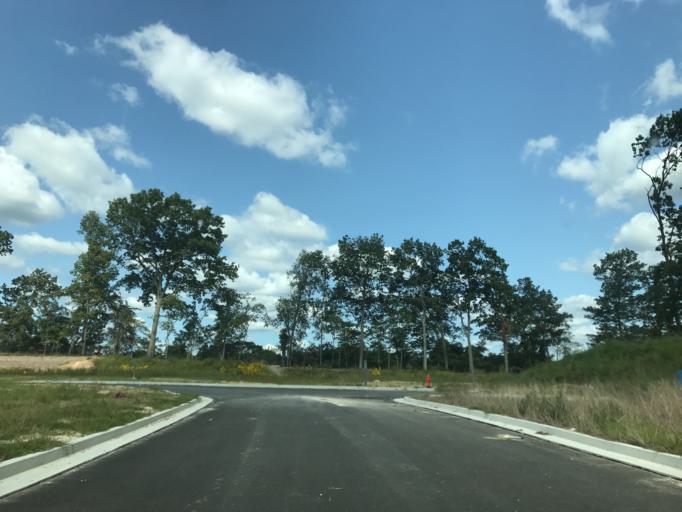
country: US
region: Maryland
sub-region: Baltimore County
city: Bowleys Quarters
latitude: 39.3610
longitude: -76.3998
